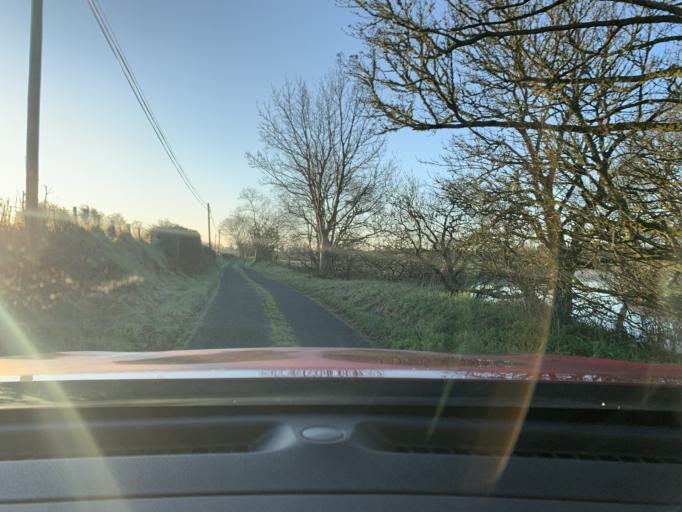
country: IE
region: Connaught
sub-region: Sligo
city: Ballymote
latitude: 54.0725
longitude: -8.5503
